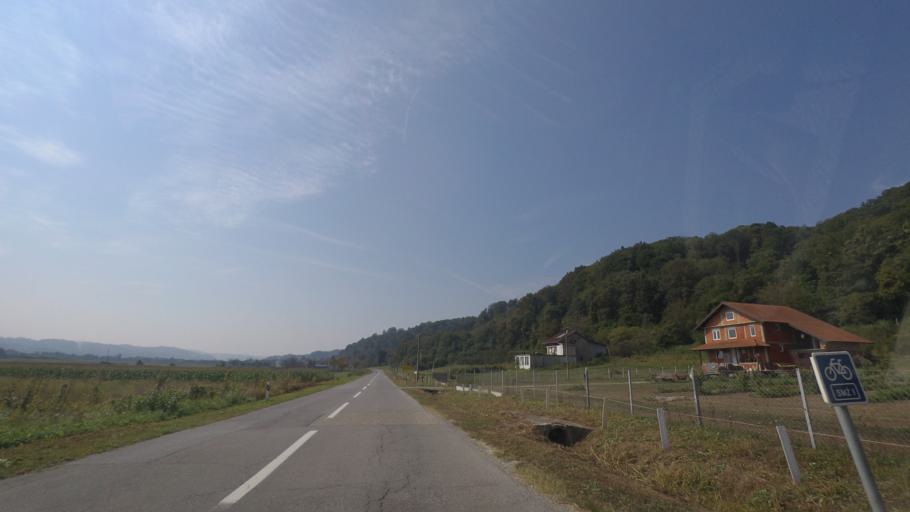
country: HR
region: Sisacko-Moslavacka
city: Dvor
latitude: 45.0974
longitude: 16.3861
